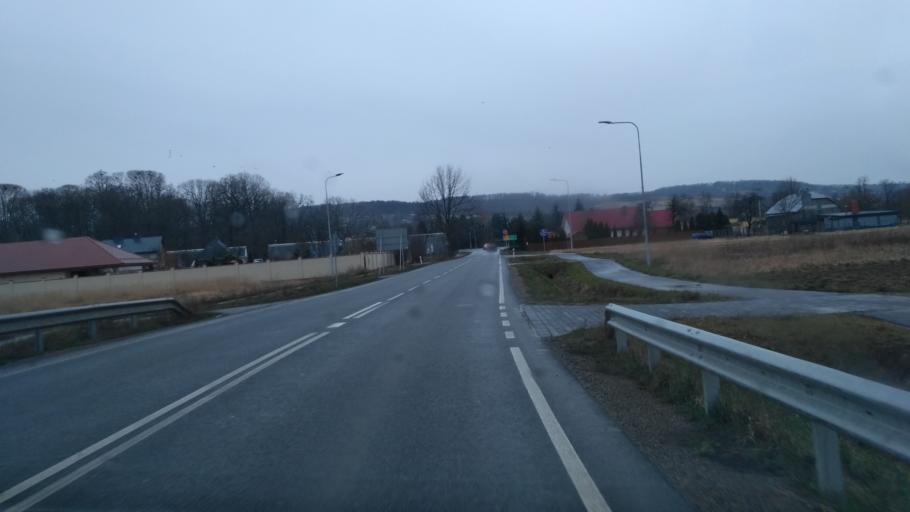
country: PL
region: Subcarpathian Voivodeship
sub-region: Powiat debicki
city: Brzeznica
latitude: 50.0611
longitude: 21.4775
